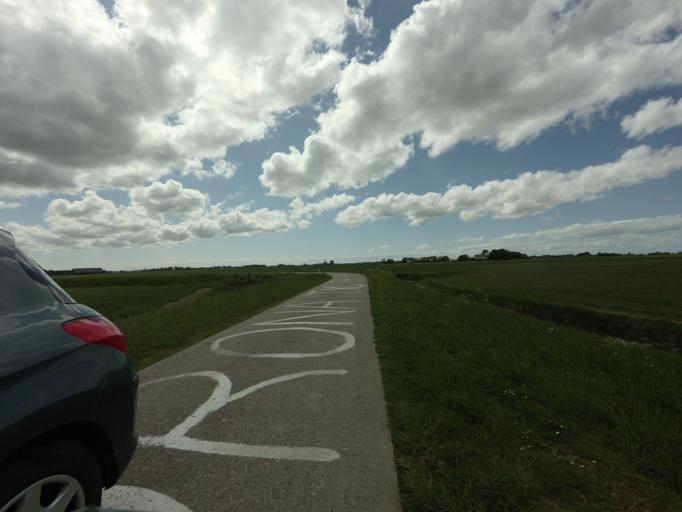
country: NL
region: Friesland
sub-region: Gemeente Franekeradeel
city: Tzum
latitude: 53.1244
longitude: 5.5547
